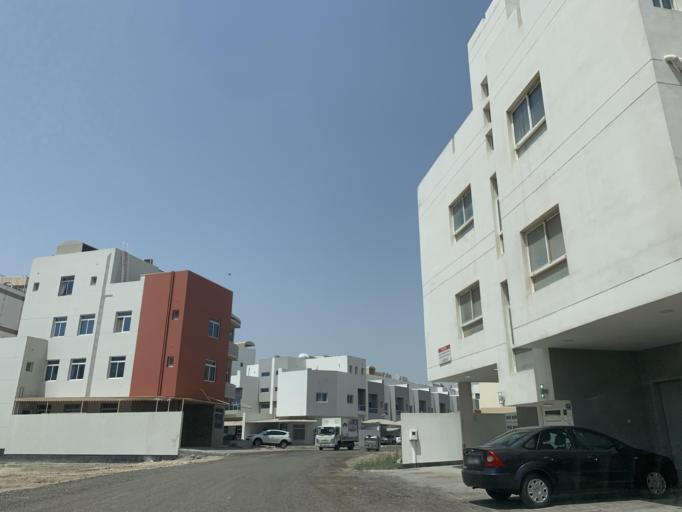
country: BH
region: Manama
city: Jidd Hafs
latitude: 26.1993
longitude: 50.5634
